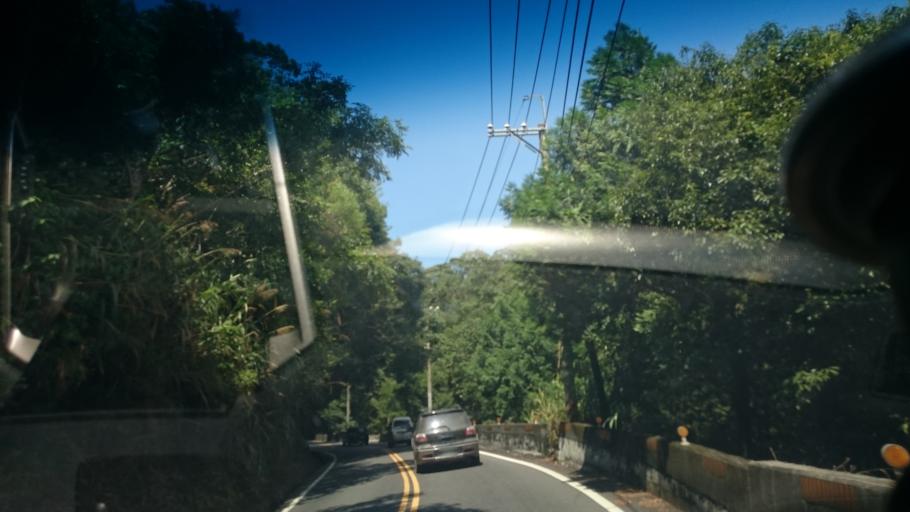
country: TW
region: Taiwan
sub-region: Nantou
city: Puli
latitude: 24.0262
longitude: 121.1417
